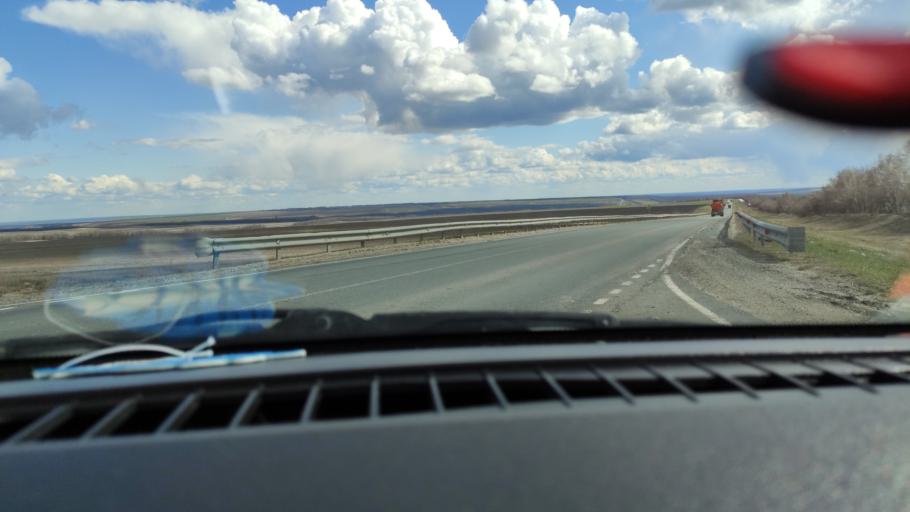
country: RU
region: Saratov
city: Dukhovnitskoye
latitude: 52.7833
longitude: 48.2337
